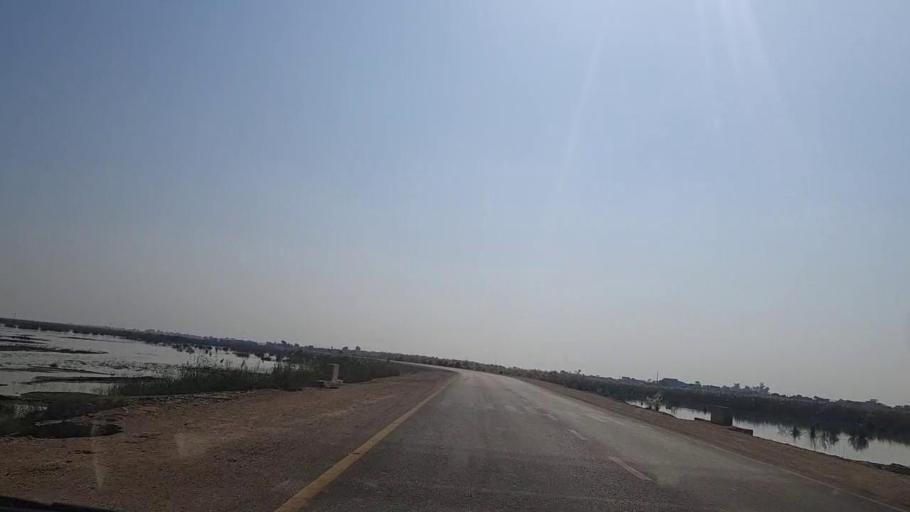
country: PK
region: Sindh
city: Sakrand
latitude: 26.0822
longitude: 68.4026
